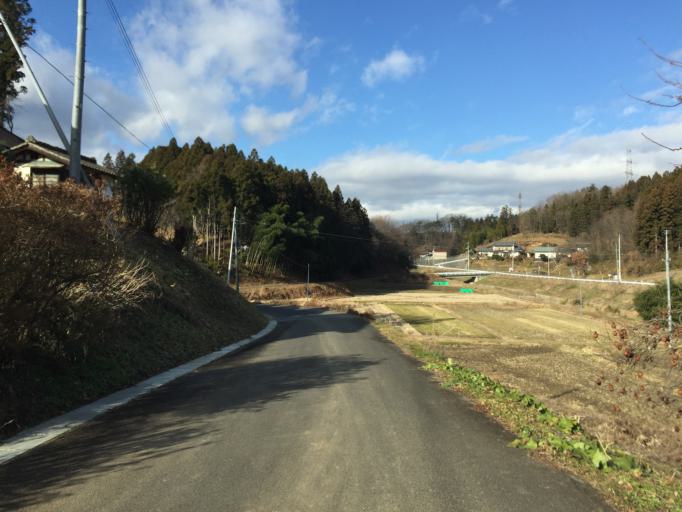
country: JP
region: Fukushima
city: Fukushima-shi
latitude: 37.6812
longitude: 140.4860
